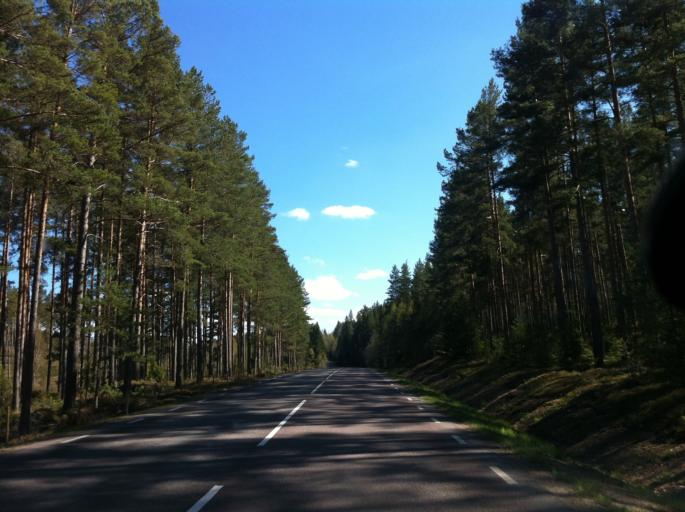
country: SE
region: Kalmar
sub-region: Hultsfreds Kommun
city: Virserum
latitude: 57.4585
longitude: 15.6596
